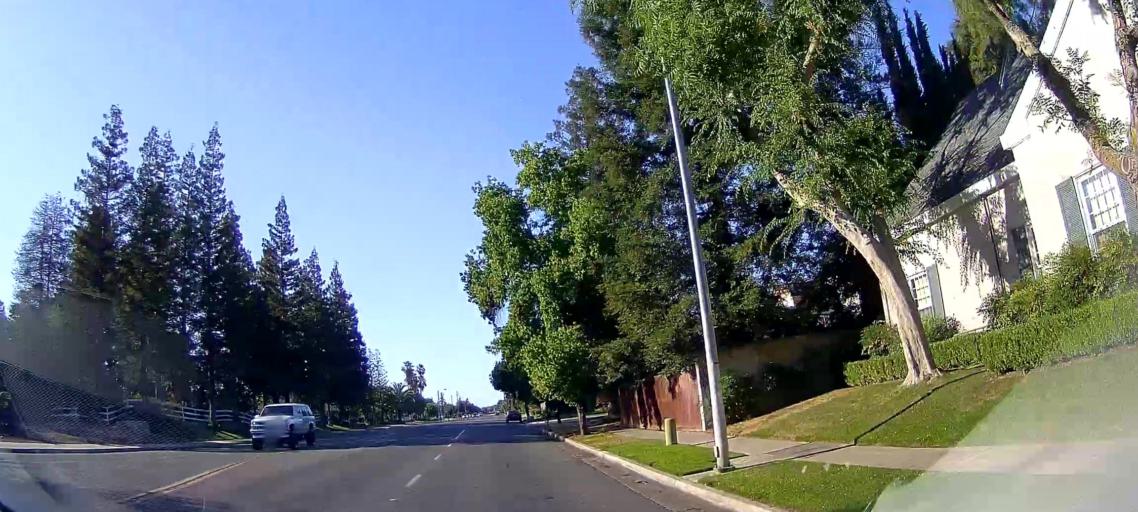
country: US
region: California
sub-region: Fresno County
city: Fresno
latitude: 36.8307
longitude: -119.7992
